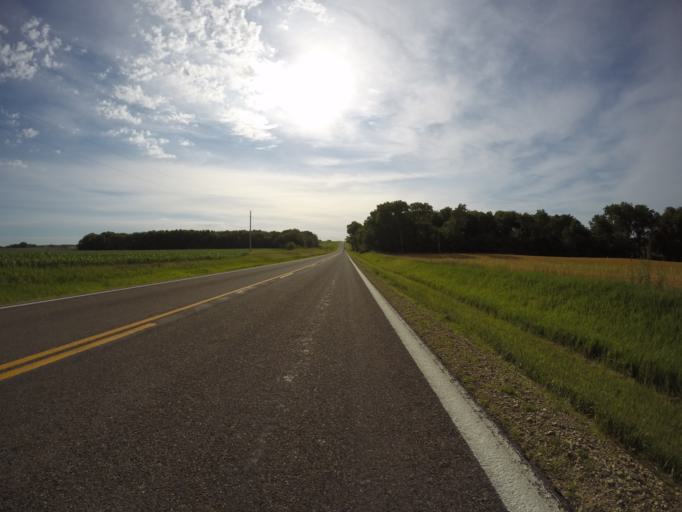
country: US
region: Kansas
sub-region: Republic County
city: Belleville
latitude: 39.7120
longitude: -97.4024
